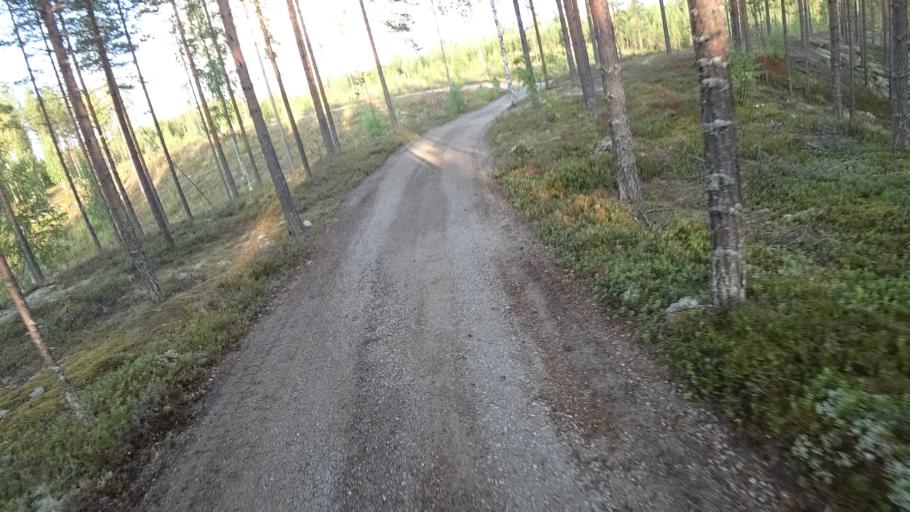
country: FI
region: North Karelia
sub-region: Joensuu
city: Ilomantsi
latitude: 62.6335
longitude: 31.0797
